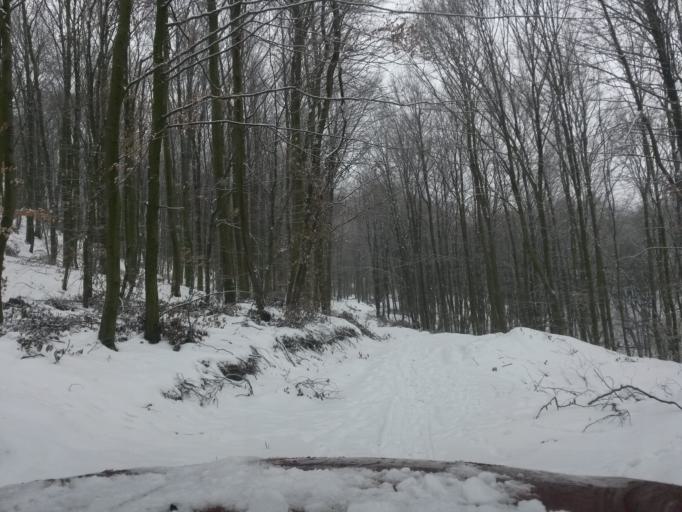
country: SK
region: Kosicky
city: Kosice
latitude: 48.7170
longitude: 21.3291
